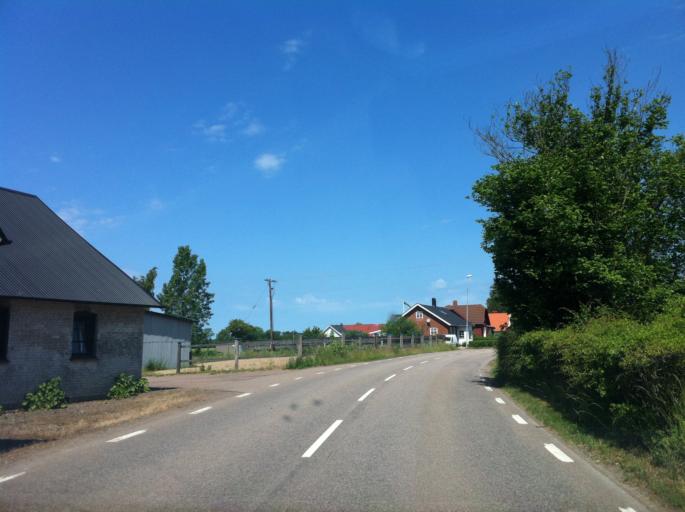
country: SE
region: Skane
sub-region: Helsingborg
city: Glumslov
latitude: 55.9630
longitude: 12.8423
